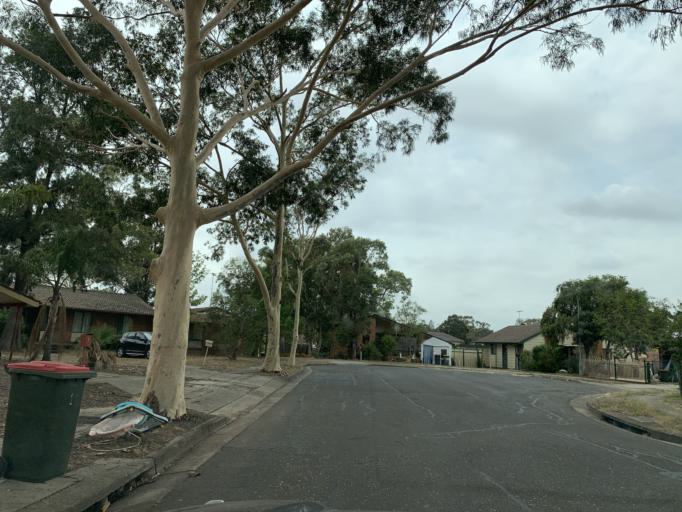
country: AU
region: New South Wales
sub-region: Blacktown
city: Doonside
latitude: -33.7527
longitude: 150.8754
